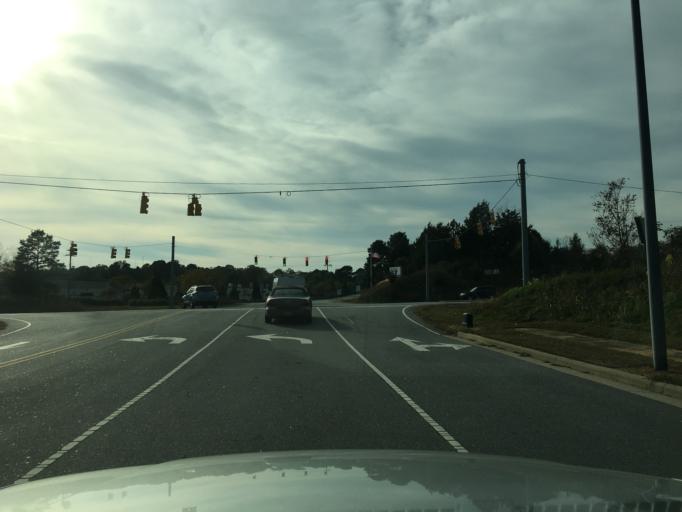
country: US
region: North Carolina
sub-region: Catawba County
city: Saint Stephens
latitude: 35.7310
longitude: -81.2901
